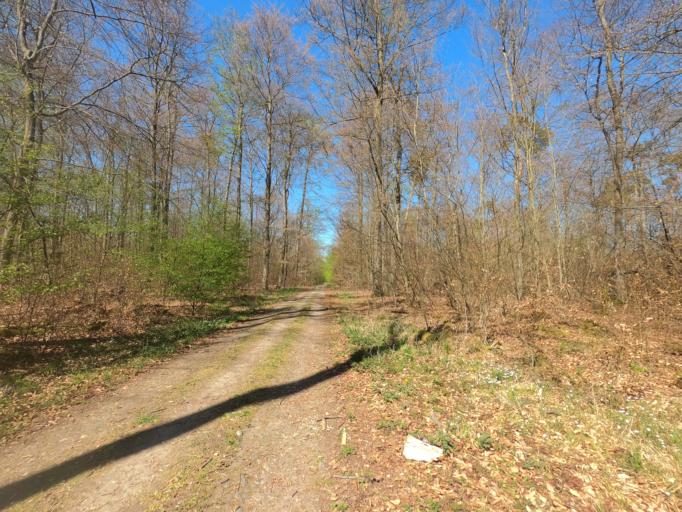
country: DE
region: Hesse
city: Morfelden-Walldorf
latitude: 49.9574
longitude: 8.5708
